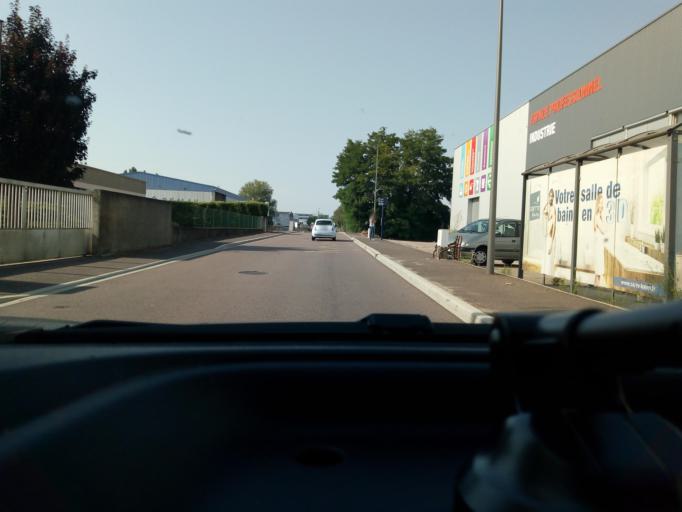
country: FR
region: Haute-Normandie
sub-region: Departement de la Seine-Maritime
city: Saint-Etienne-du-Rouvray
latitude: 49.3993
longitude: 1.1147
